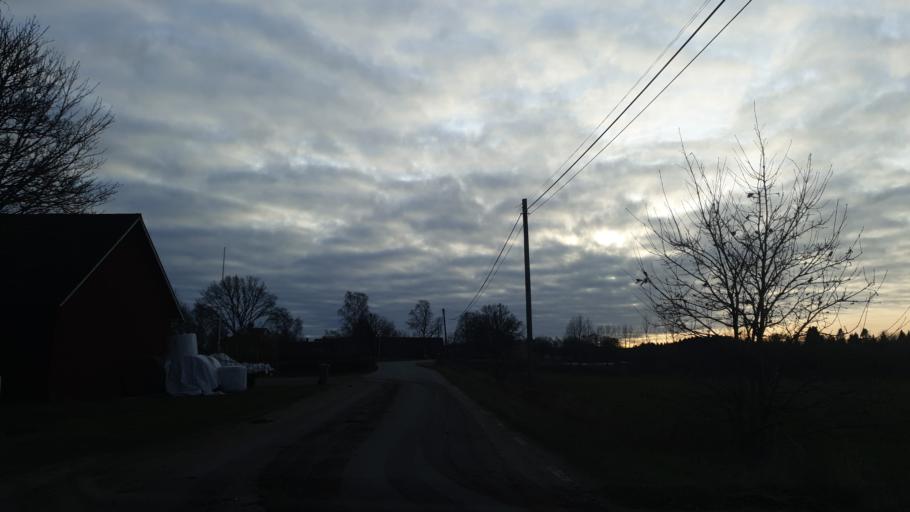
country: SE
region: Blekinge
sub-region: Karlskrona Kommun
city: Jaemjoe
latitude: 56.1857
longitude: 15.9423
